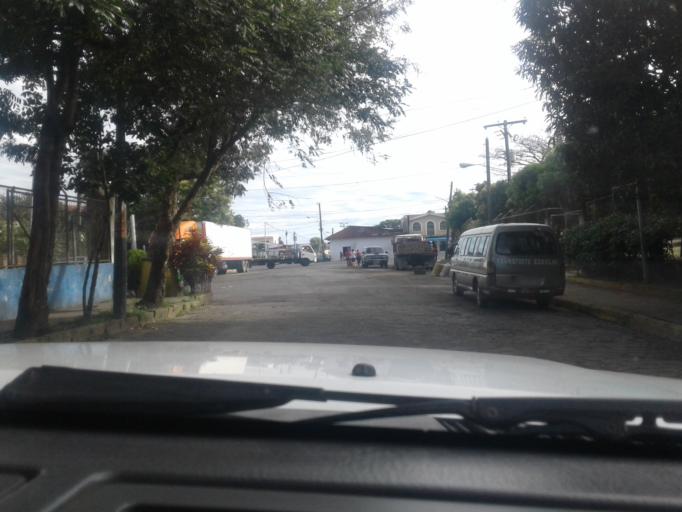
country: NI
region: Carazo
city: Jinotepe
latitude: 11.8523
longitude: -86.2032
